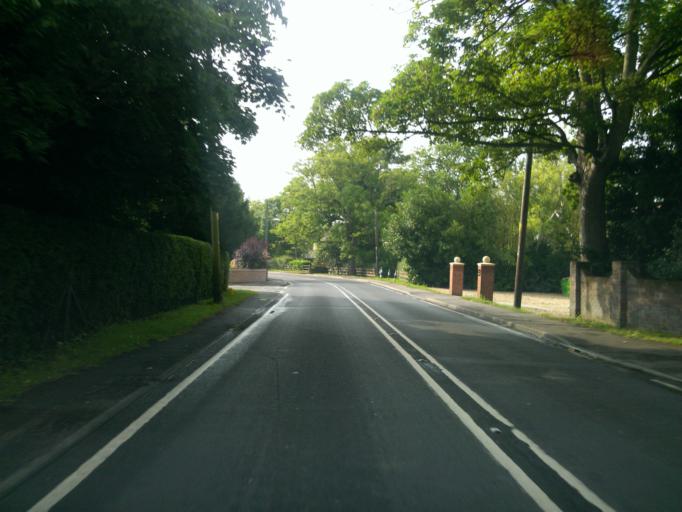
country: GB
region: England
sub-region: Essex
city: Little Clacton
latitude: 51.8408
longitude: 1.1294
